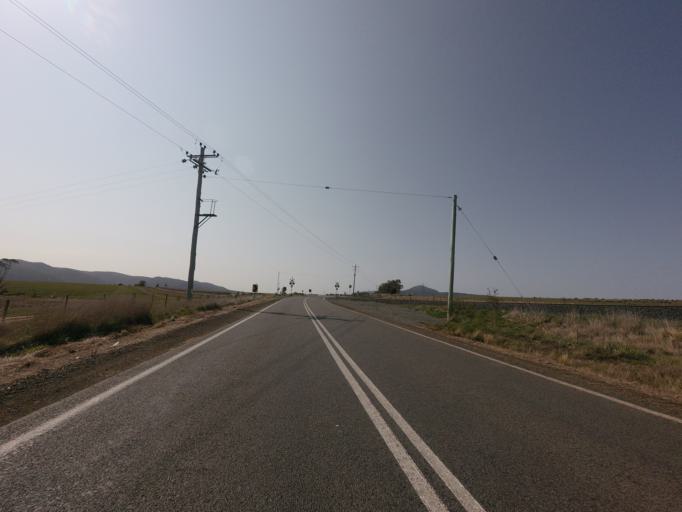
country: AU
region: Tasmania
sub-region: Northern Midlands
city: Evandale
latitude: -41.7979
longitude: 147.7030
